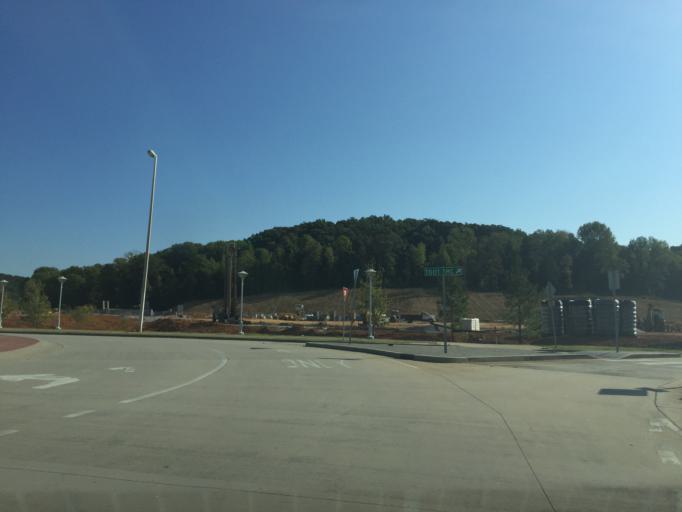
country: US
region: Tennessee
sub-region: Hamilton County
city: Harrison
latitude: 35.0730
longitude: -85.1318
